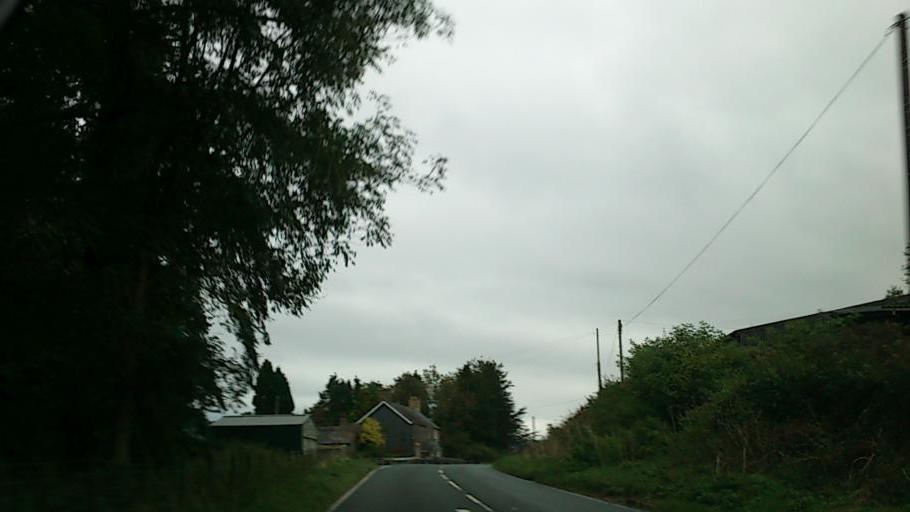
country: GB
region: Wales
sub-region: Gwynedd
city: Corris
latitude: 52.6804
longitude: -3.6992
